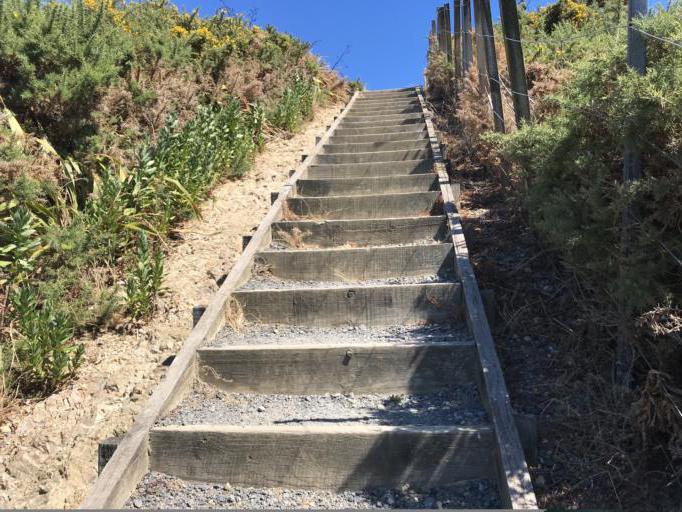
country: NZ
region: Wellington
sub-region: Wellington City
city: Brooklyn
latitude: -41.3319
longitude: 174.7663
